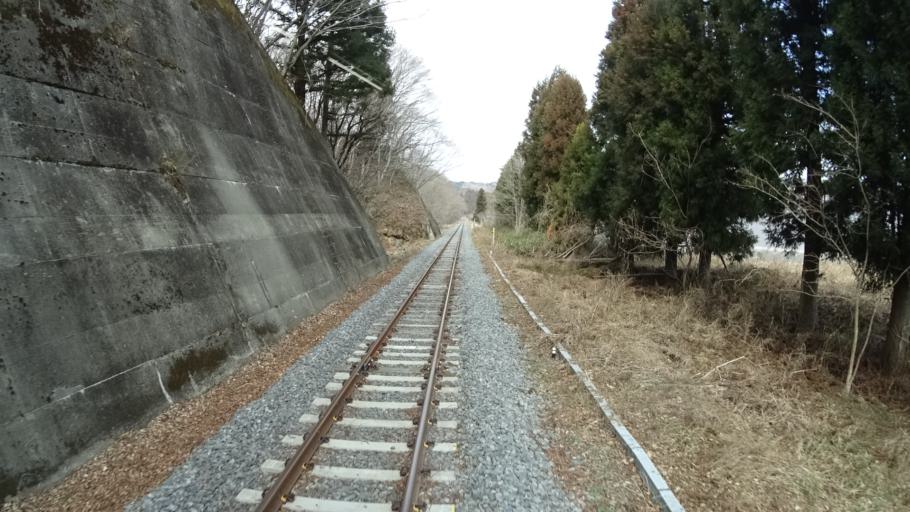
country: JP
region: Iwate
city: Miyako
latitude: 39.5572
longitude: 141.9396
